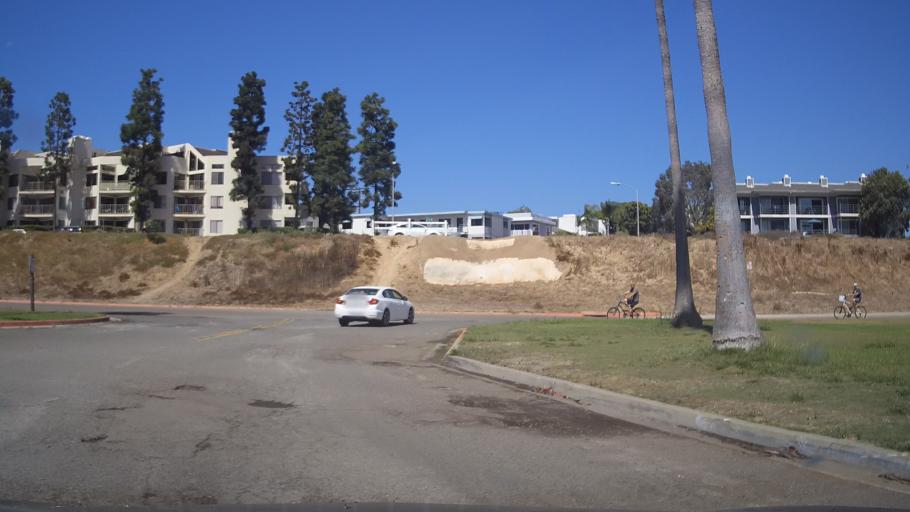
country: US
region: California
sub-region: San Diego County
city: La Jolla
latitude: 32.7889
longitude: -117.2333
